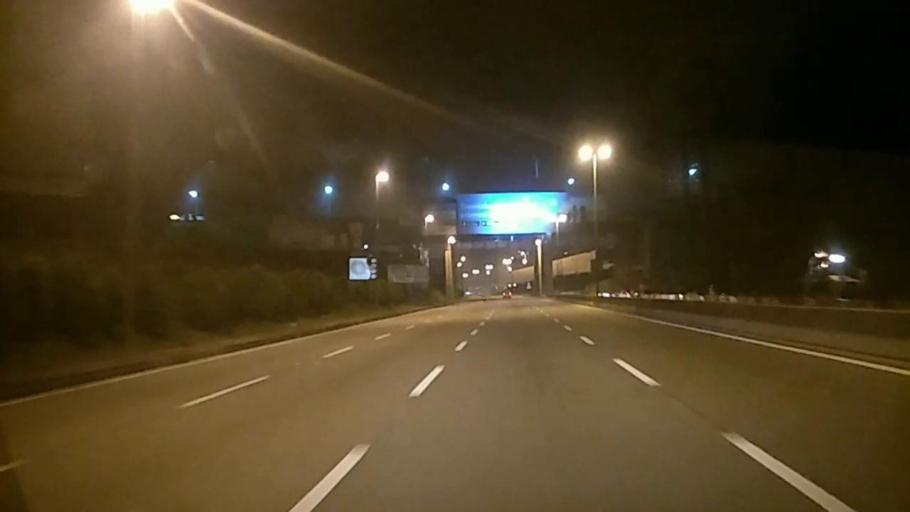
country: MY
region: Selangor
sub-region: Petaling
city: Petaling Jaya
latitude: 3.1846
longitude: 101.6195
